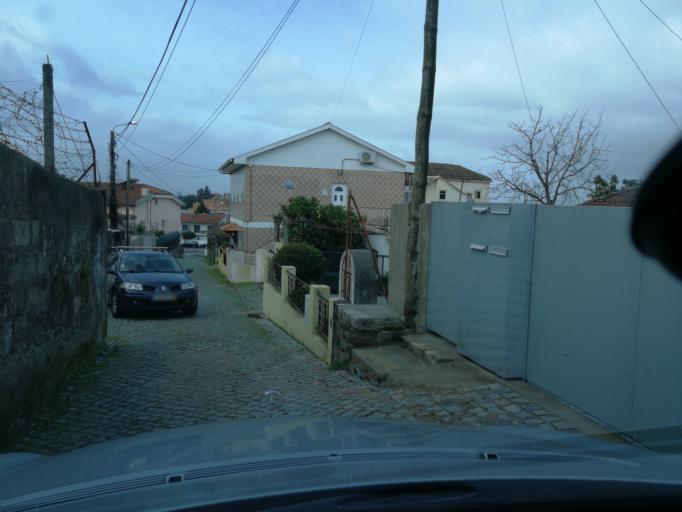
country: PT
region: Braga
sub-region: Braga
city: Braga
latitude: 41.5312
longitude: -8.4150
